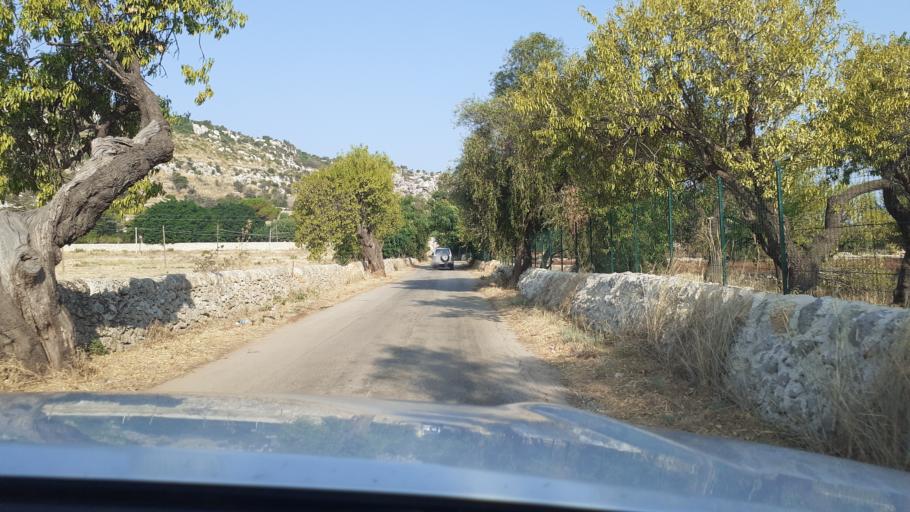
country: IT
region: Sicily
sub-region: Provincia di Siracusa
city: Cassibile
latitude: 36.9775
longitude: 15.1781
